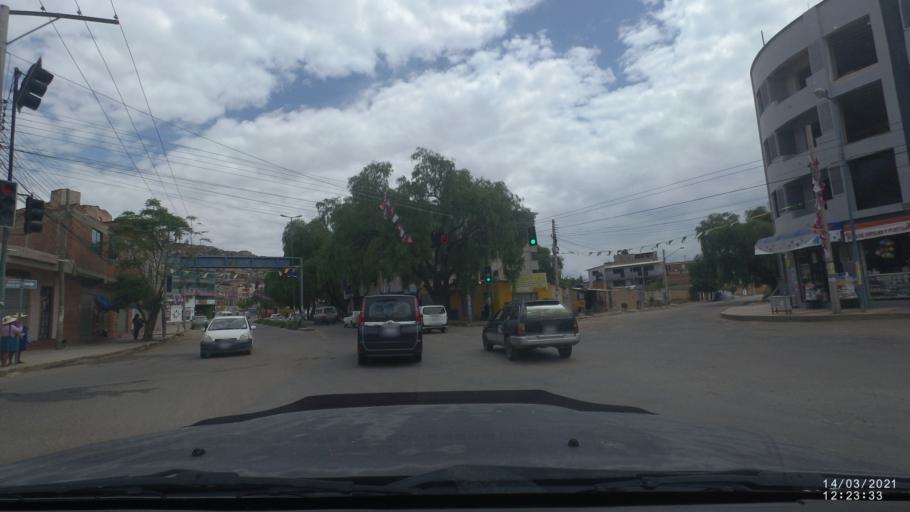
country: BO
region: Cochabamba
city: Cochabamba
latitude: -17.4238
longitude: -66.1344
